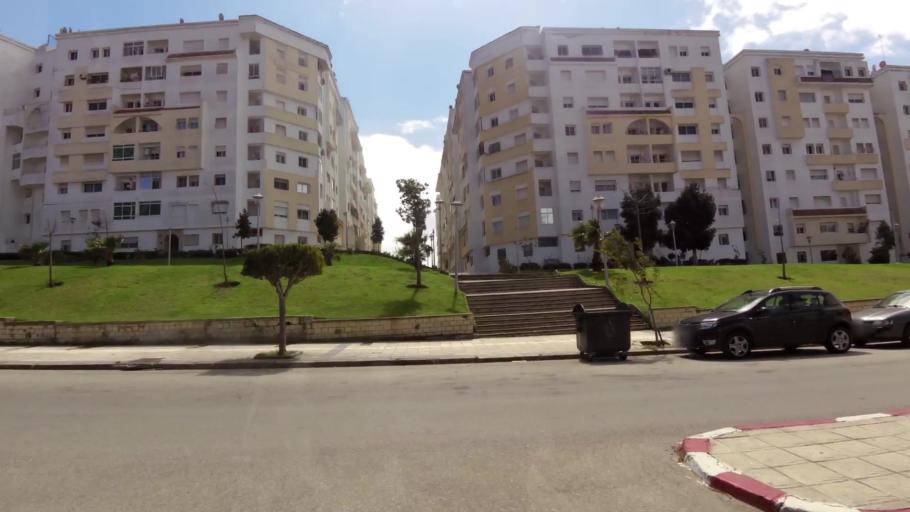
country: MA
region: Tanger-Tetouan
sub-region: Tanger-Assilah
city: Tangier
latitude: 35.7664
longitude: -5.8328
